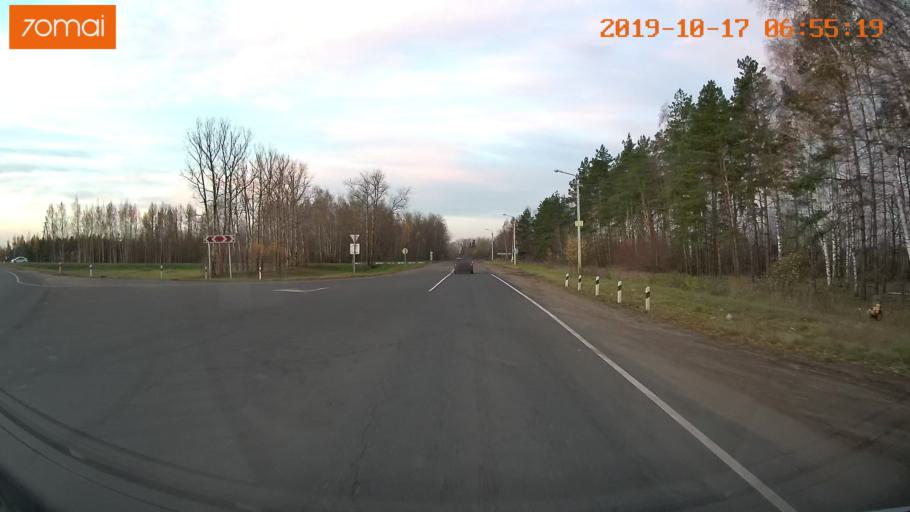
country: RU
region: Vladimir
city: Suzdal'
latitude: 56.4569
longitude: 40.4588
